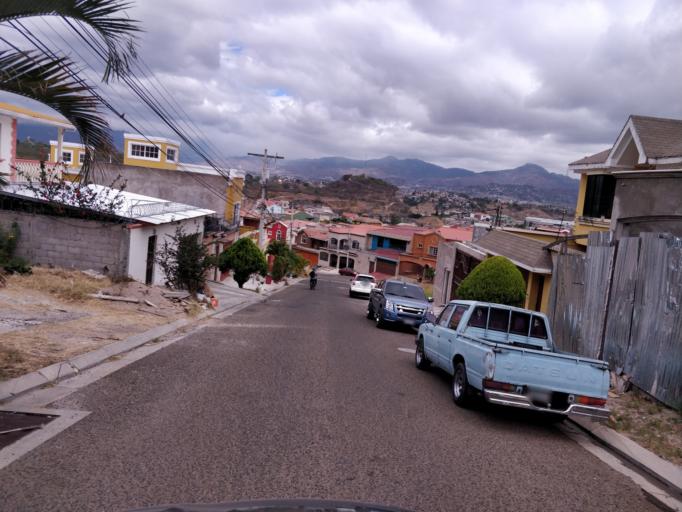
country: HN
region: Francisco Morazan
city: Yaguacire
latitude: 14.0474
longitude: -87.2173
